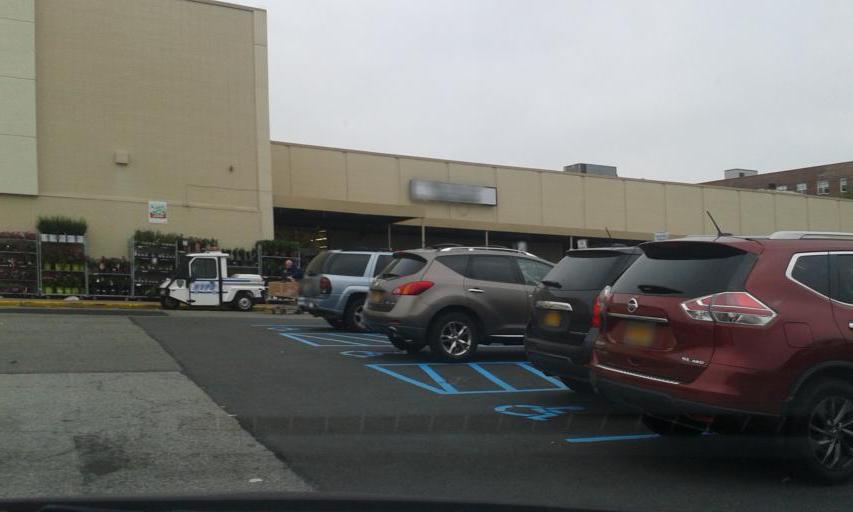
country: US
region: New York
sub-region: Richmond County
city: Staten Island
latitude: 40.5658
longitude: -74.1114
